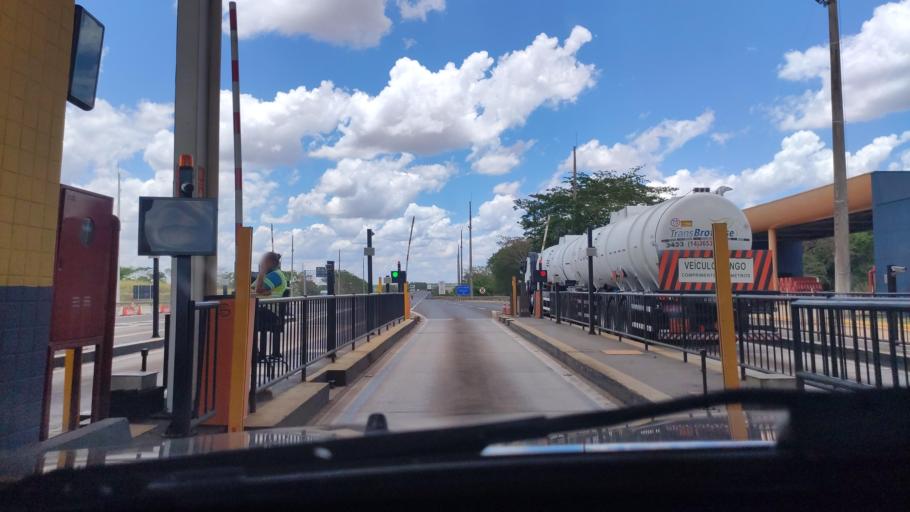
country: BR
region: Sao Paulo
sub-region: Pederneiras
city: Pederneiras
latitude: -22.3182
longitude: -48.7256
